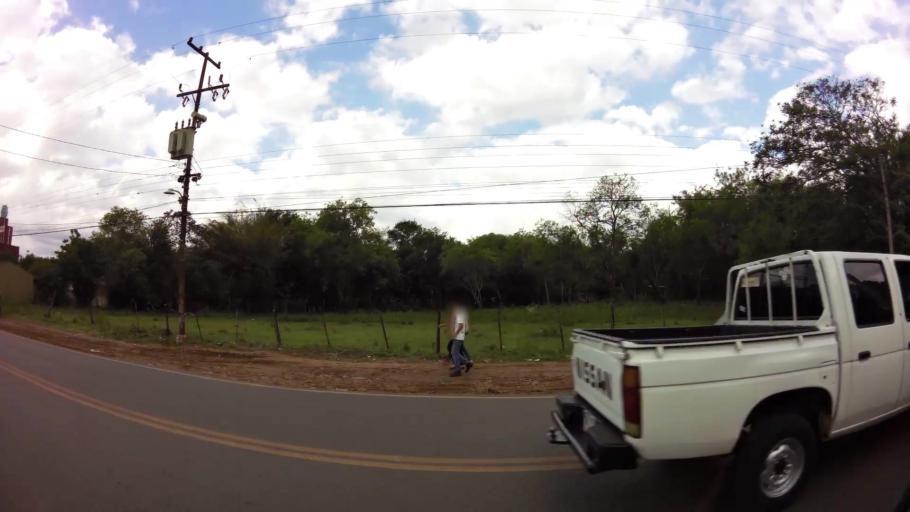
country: PY
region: Central
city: San Lorenzo
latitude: -25.2757
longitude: -57.4860
